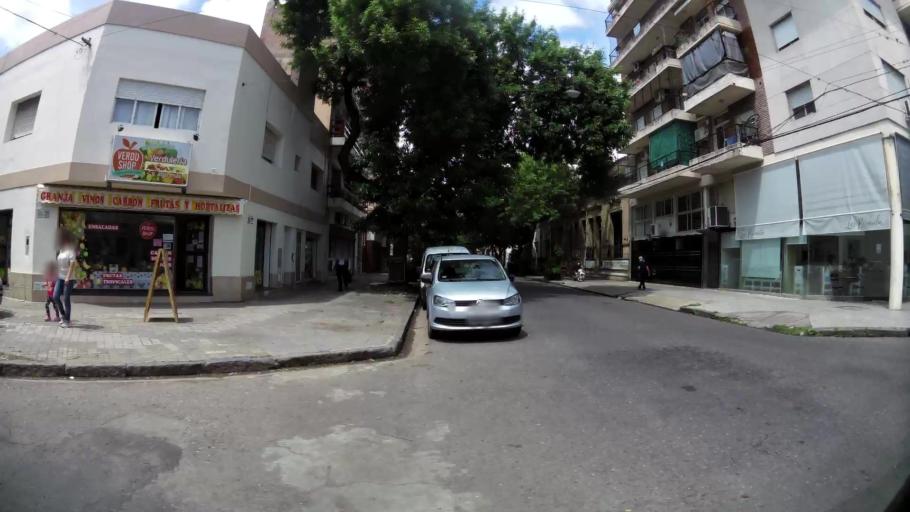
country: AR
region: Santa Fe
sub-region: Departamento de Rosario
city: Rosario
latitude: -32.9600
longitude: -60.6328
